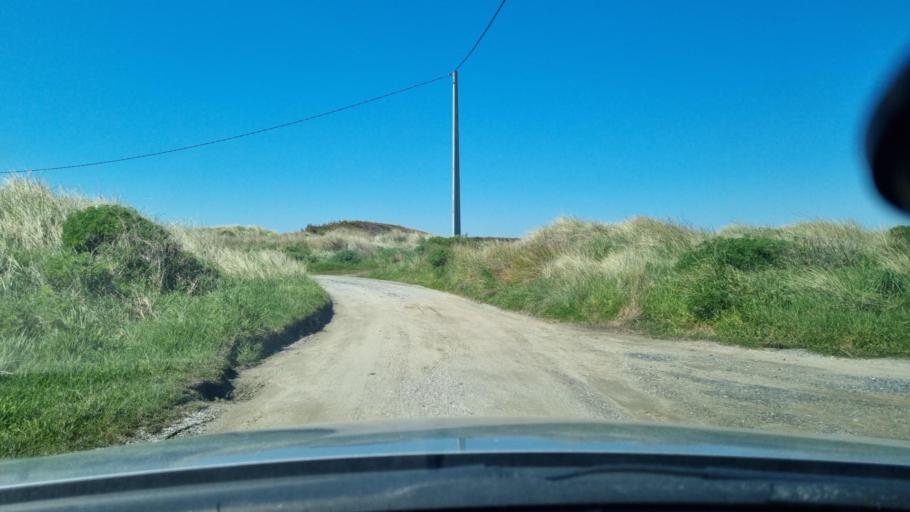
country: NZ
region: Southland
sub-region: Invercargill City
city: Invercargill
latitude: -46.4299
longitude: 168.2290
